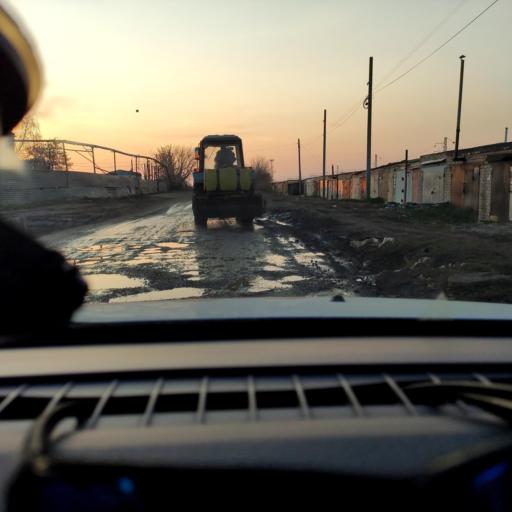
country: RU
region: Samara
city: Samara
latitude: 53.1814
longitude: 50.1447
